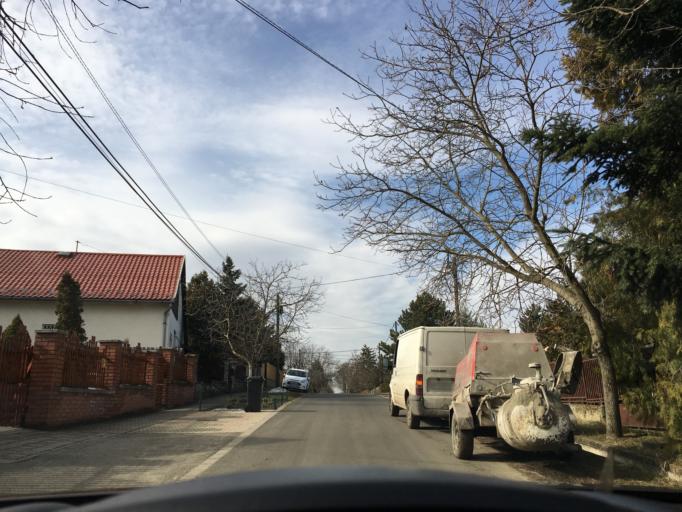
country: HU
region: Budapest
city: Budapest XVII. keruelet
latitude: 47.4762
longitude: 19.2842
